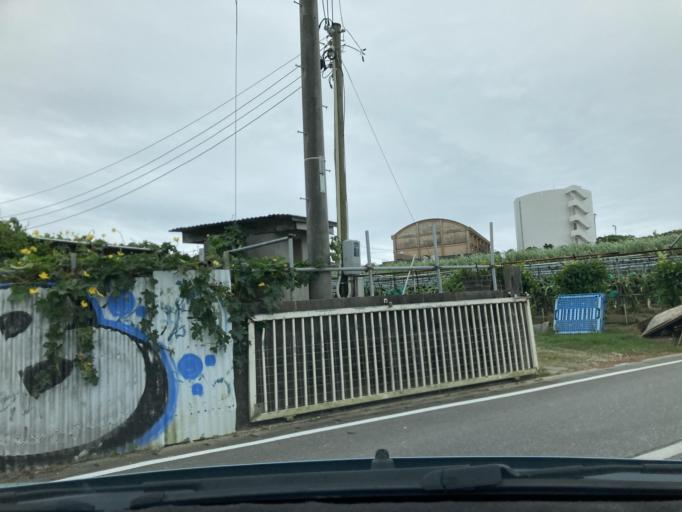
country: JP
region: Okinawa
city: Tomigusuku
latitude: 26.1581
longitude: 127.7021
